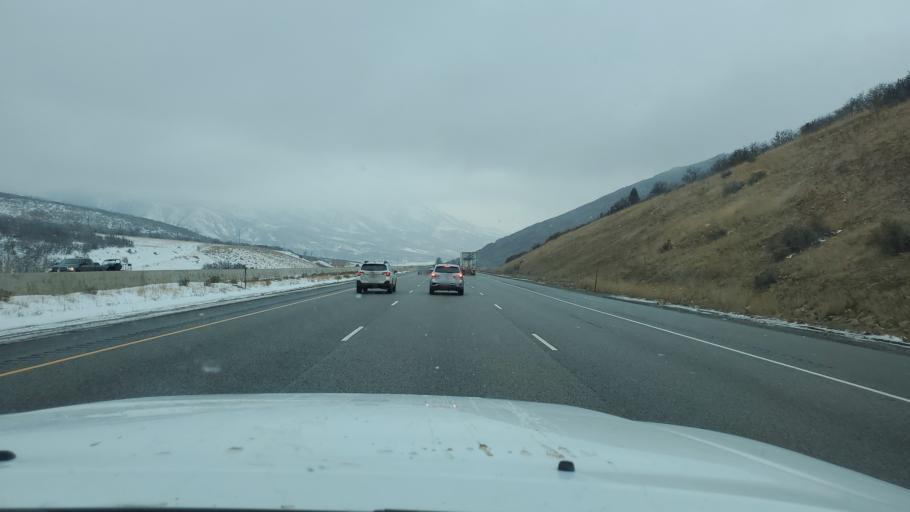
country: US
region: Utah
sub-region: Summit County
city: Summit Park
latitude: 40.7463
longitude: -111.6413
